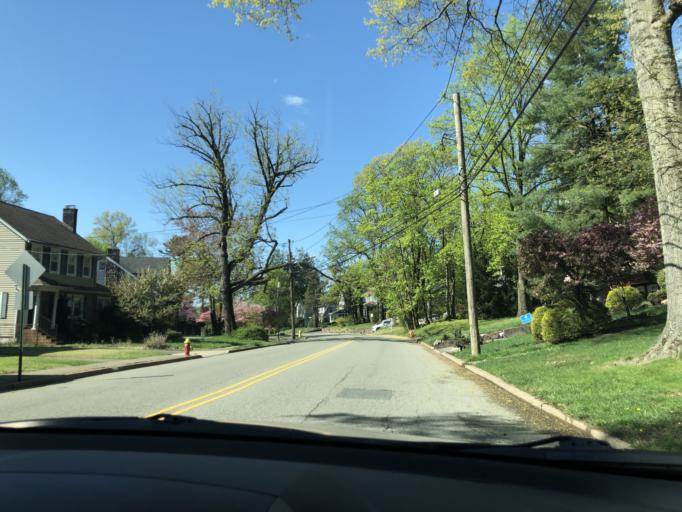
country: US
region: New Jersey
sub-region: Essex County
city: Caldwell
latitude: 40.8415
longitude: -74.2633
